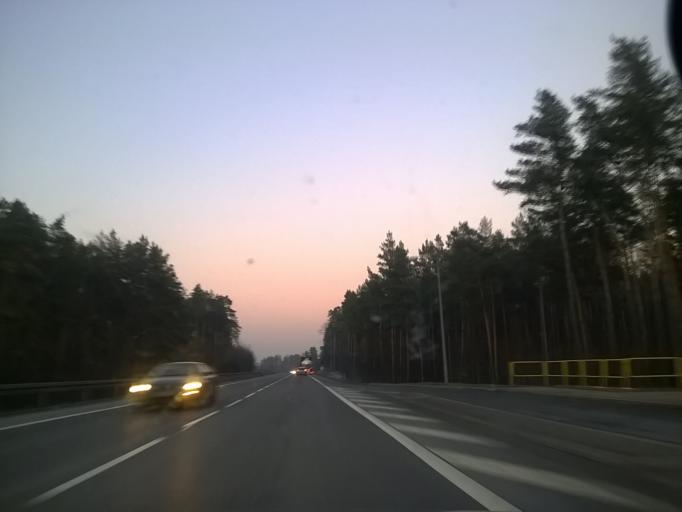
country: PL
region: Warmian-Masurian Voivodeship
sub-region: Powiat olsztynski
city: Barczewo
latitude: 53.7981
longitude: 20.6152
